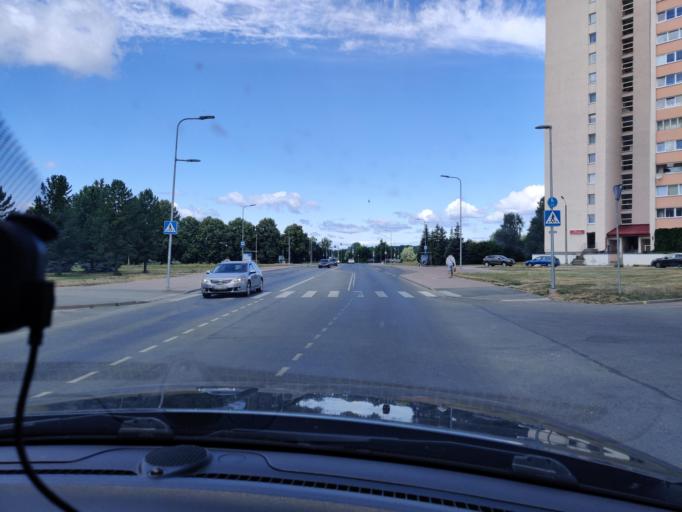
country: EE
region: Harju
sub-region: Saue vald
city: Laagri
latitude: 59.4084
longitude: 24.6329
